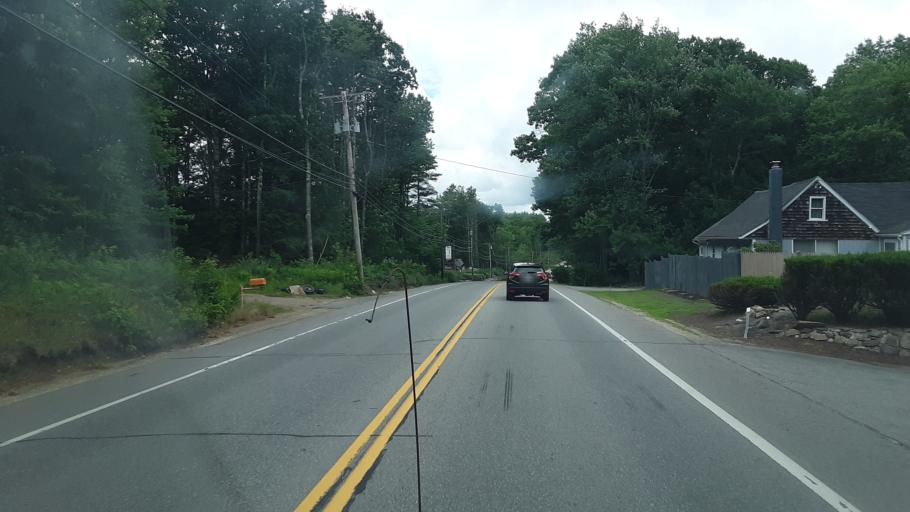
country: US
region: New Hampshire
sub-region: Rockingham County
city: Northwood
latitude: 43.2205
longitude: -71.2311
